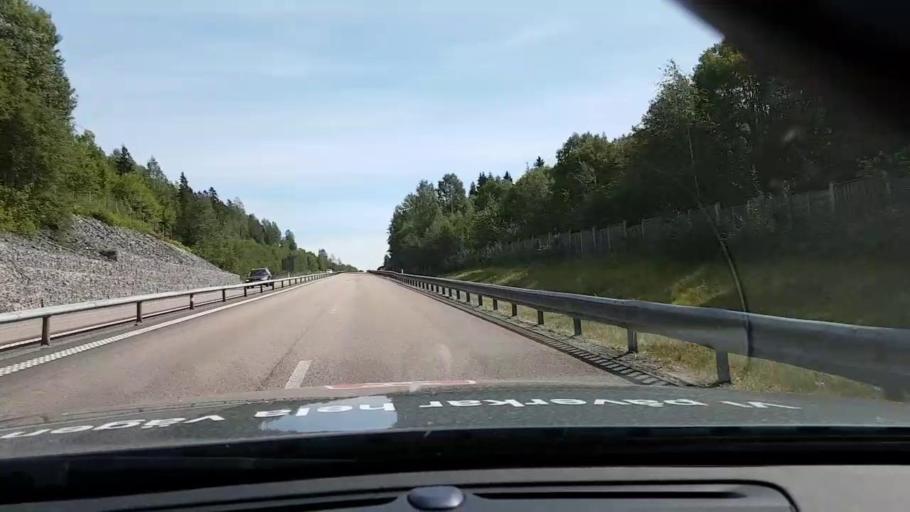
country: SE
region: Vaesternorrland
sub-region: OErnskoeldsviks Kommun
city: Ornskoldsvik
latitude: 63.3160
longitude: 18.8051
